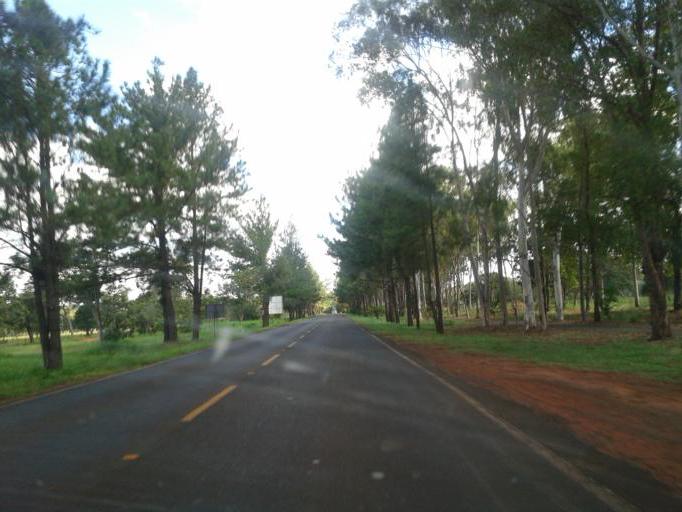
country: BR
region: Minas Gerais
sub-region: Santa Vitoria
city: Santa Vitoria
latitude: -18.8673
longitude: -50.1254
